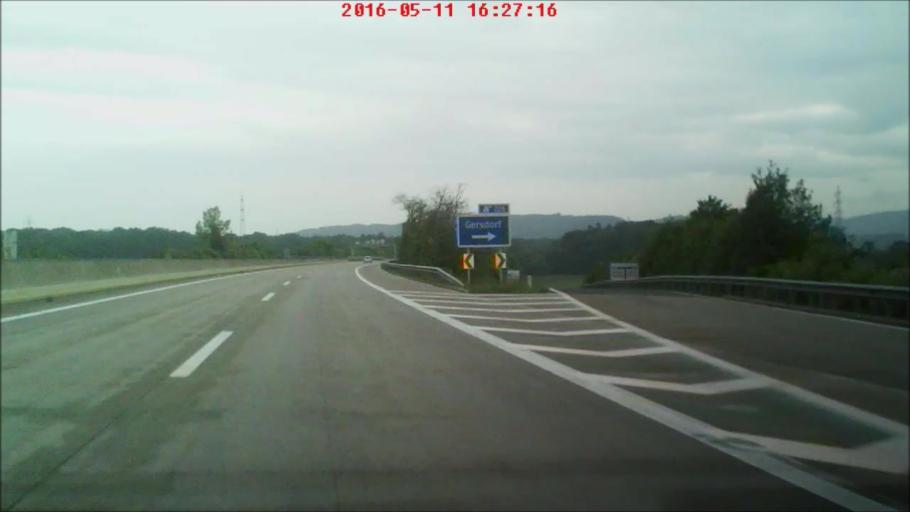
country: AT
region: Styria
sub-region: Politischer Bezirk Leibnitz
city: Strass in Steiermark
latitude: 46.7276
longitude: 15.6457
